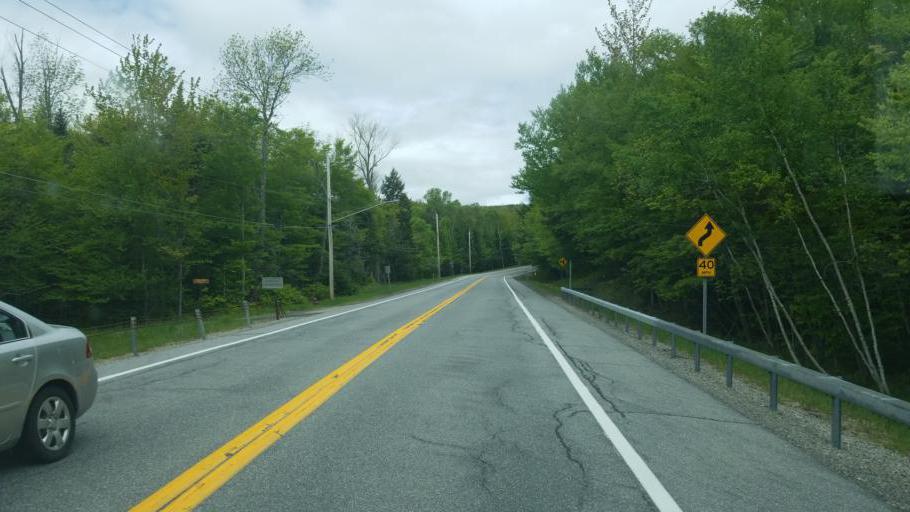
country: US
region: New York
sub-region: Franklin County
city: Tupper Lake
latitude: 43.8616
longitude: -74.4345
